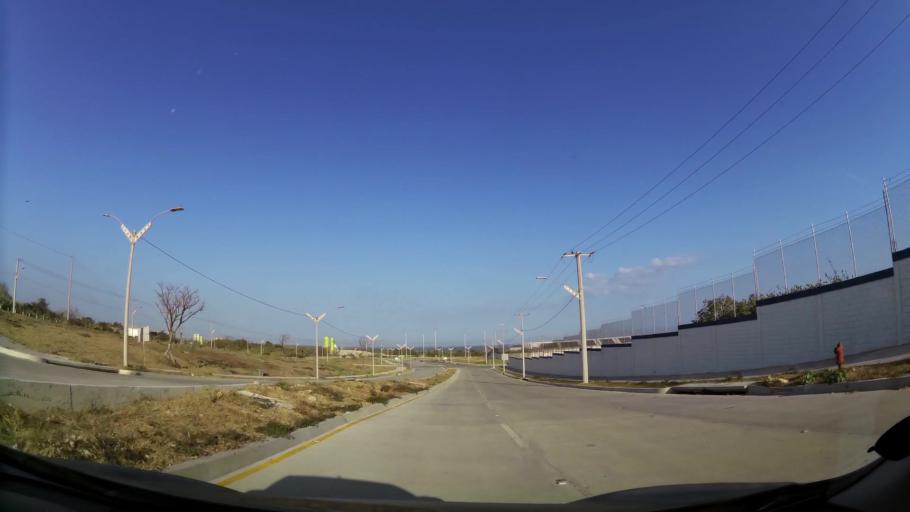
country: CO
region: Atlantico
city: Barranquilla
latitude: 11.0314
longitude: -74.8288
